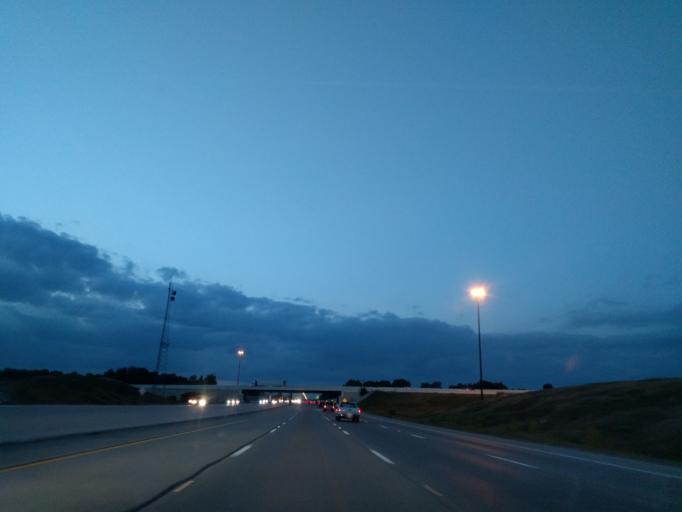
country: US
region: Indiana
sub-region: Marion County
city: Speedway
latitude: 39.8044
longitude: -86.2752
